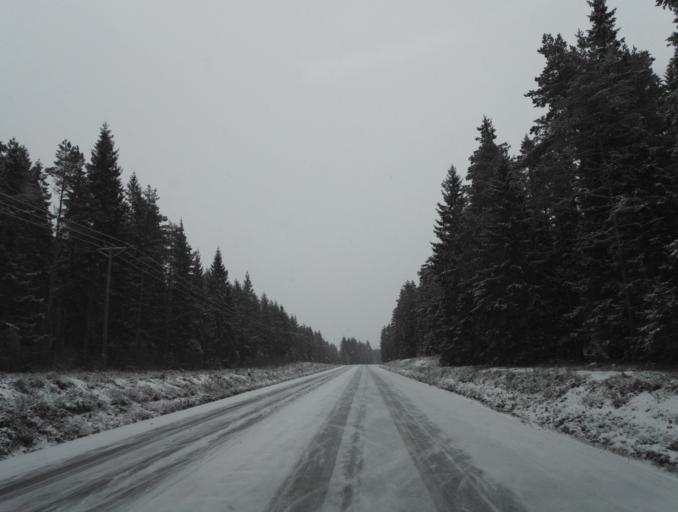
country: SE
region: Kronoberg
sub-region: Uppvidinge Kommun
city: Lenhovda
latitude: 57.0174
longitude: 15.2496
